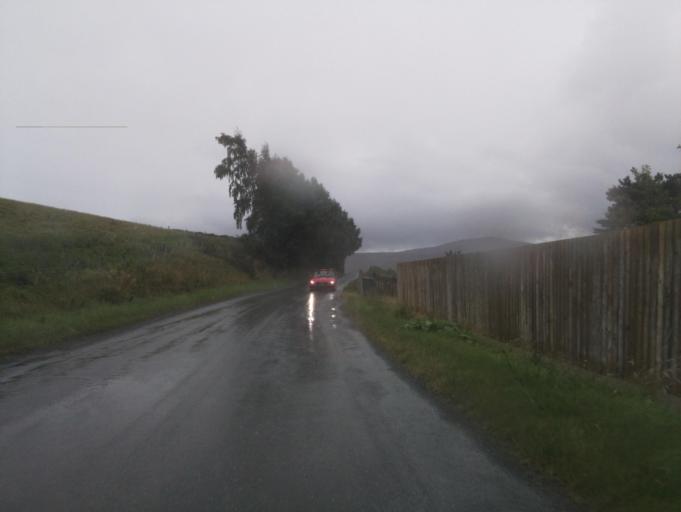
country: GB
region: Scotland
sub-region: Highland
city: Grantown on Spey
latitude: 57.3061
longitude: -3.5755
